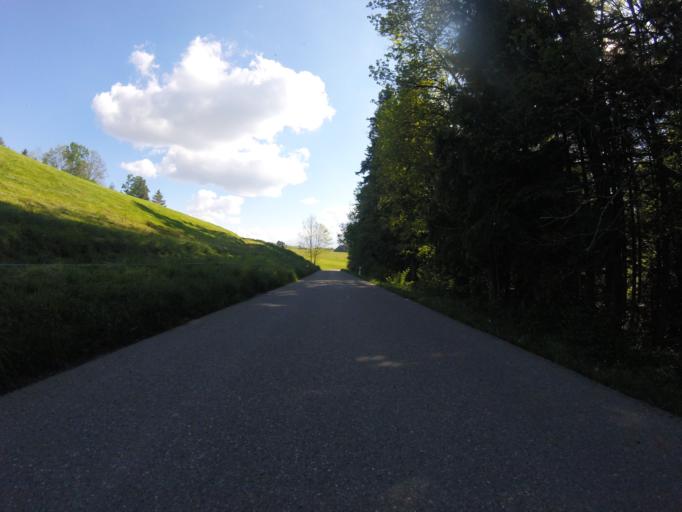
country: CH
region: Saint Gallen
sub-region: Wahlkreis Wil
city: Degersheim
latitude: 47.3921
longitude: 9.1987
